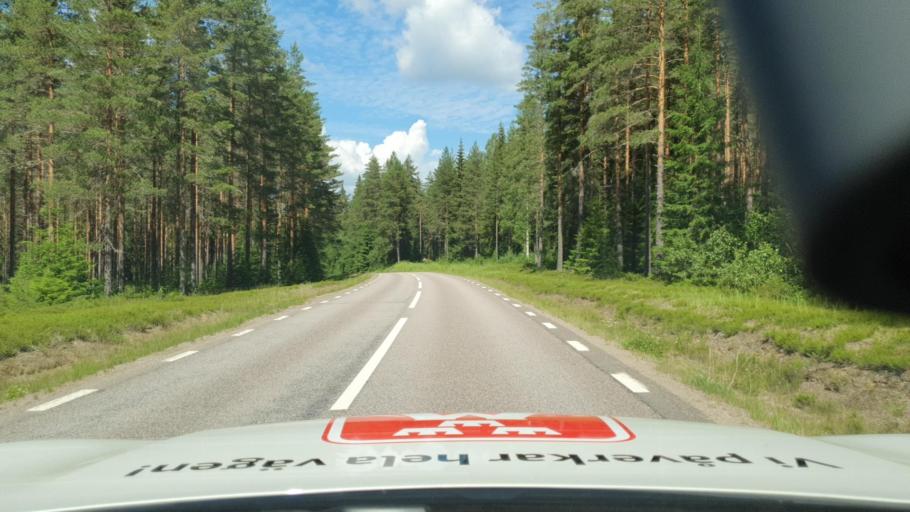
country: SE
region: Vaermland
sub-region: Torsby Kommun
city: Torsby
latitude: 60.3786
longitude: 12.9243
